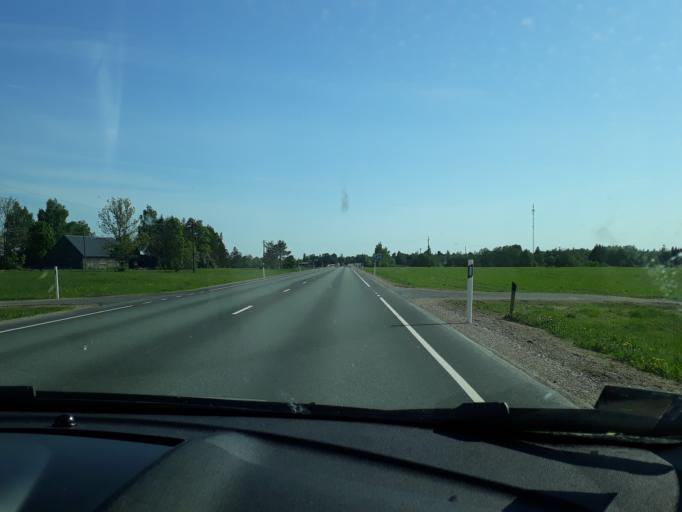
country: EE
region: Paernumaa
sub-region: Tootsi vald
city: Tootsi
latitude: 58.5280
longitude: 24.8283
